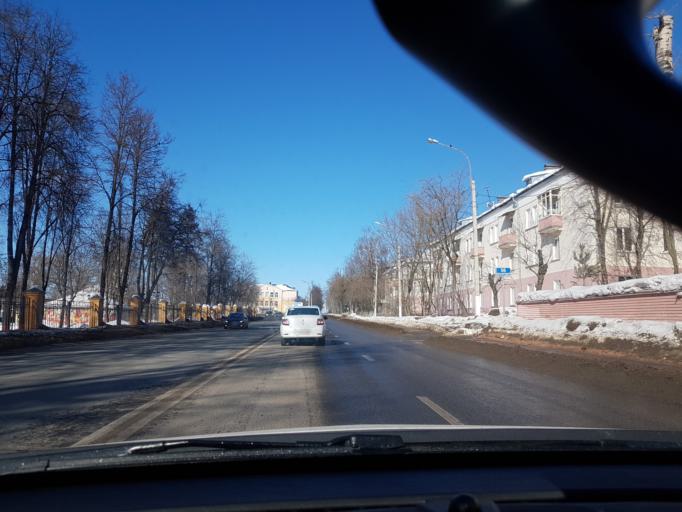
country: RU
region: Moskovskaya
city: Istra
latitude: 55.9183
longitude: 36.8586
